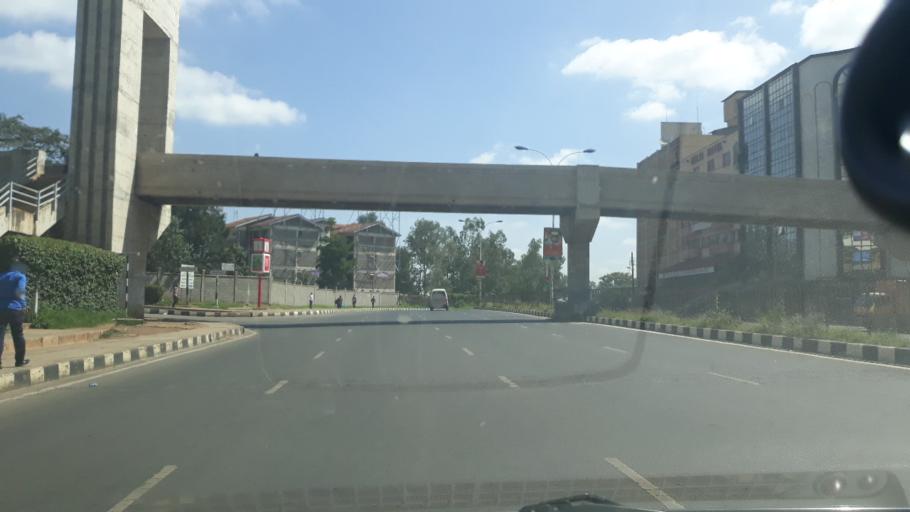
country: KE
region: Nairobi Area
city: Nairobi
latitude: -1.2803
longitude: 36.8178
